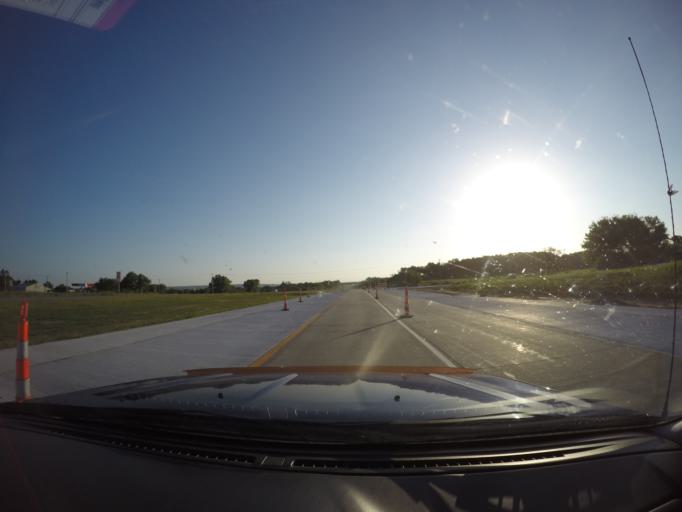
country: US
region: Kansas
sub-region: Pottawatomie County
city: Wamego
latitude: 39.2011
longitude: -96.4389
